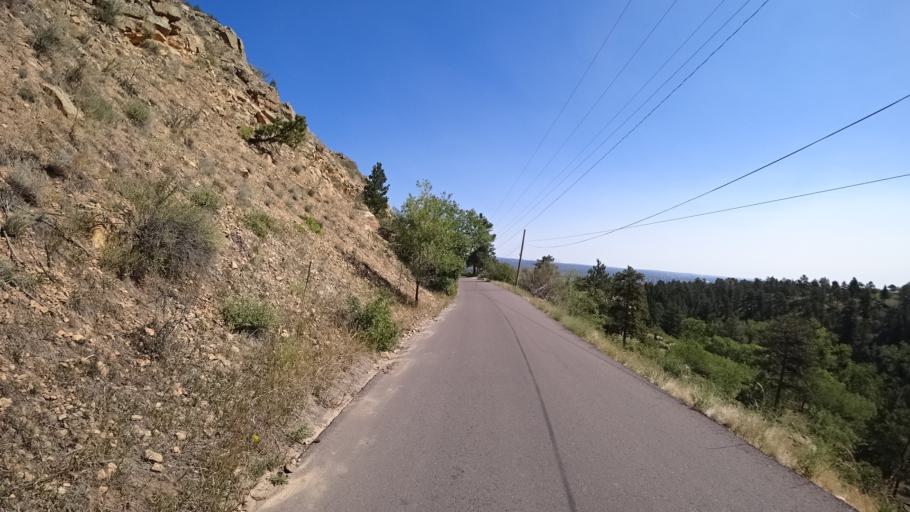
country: US
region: Colorado
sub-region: El Paso County
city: Manitou Springs
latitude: 38.8243
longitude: -104.8874
